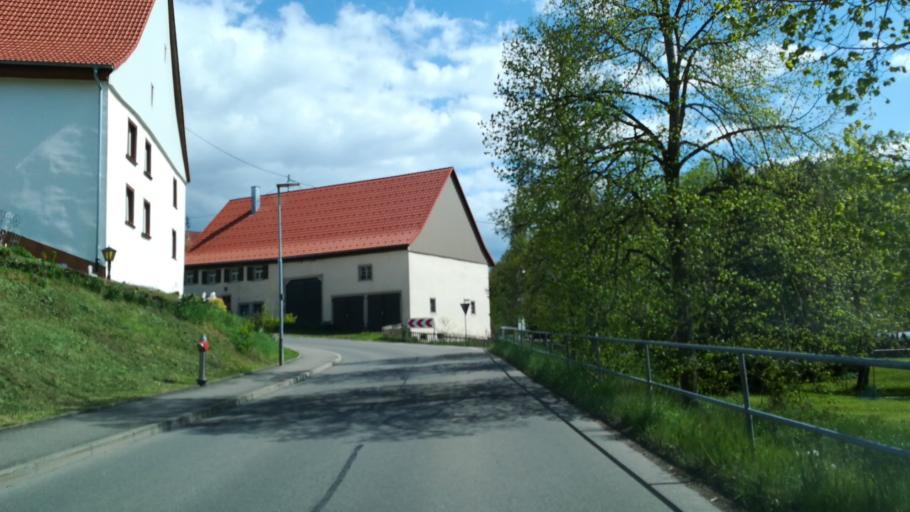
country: DE
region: Baden-Wuerttemberg
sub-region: Freiburg Region
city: Blumberg
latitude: 47.8369
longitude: 8.5002
